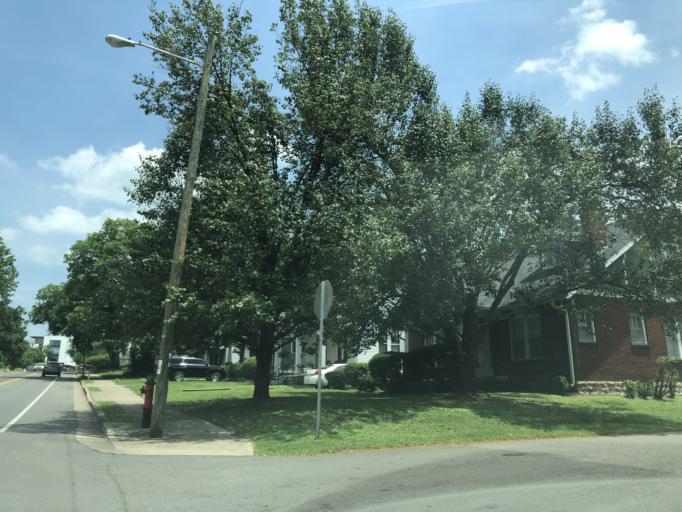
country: US
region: Tennessee
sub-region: Davidson County
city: Nashville
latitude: 36.1841
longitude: -86.7531
